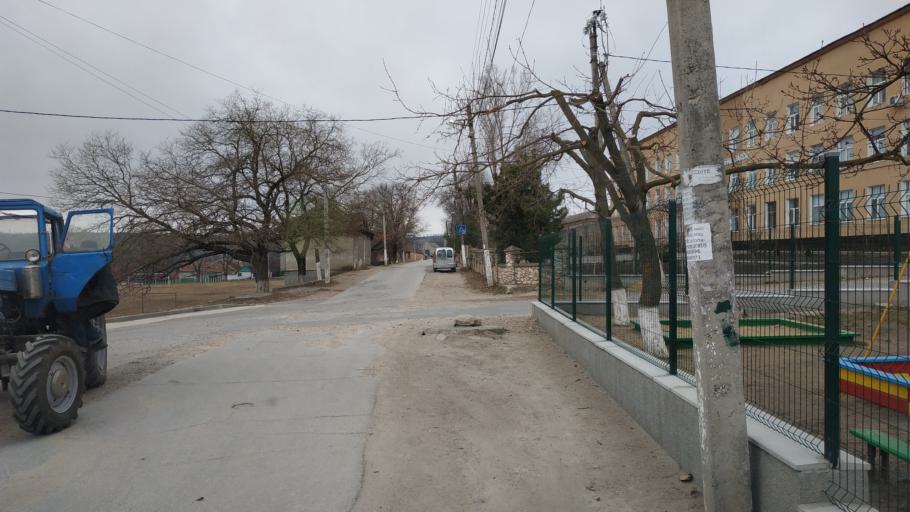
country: MD
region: Laloveni
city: Ialoveni
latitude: 46.9092
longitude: 28.8051
